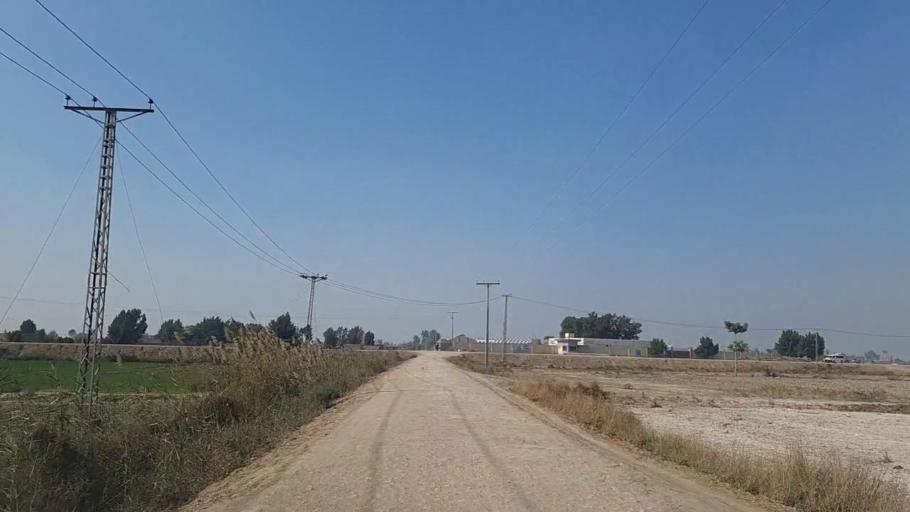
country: PK
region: Sindh
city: Daur
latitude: 26.4526
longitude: 68.3085
